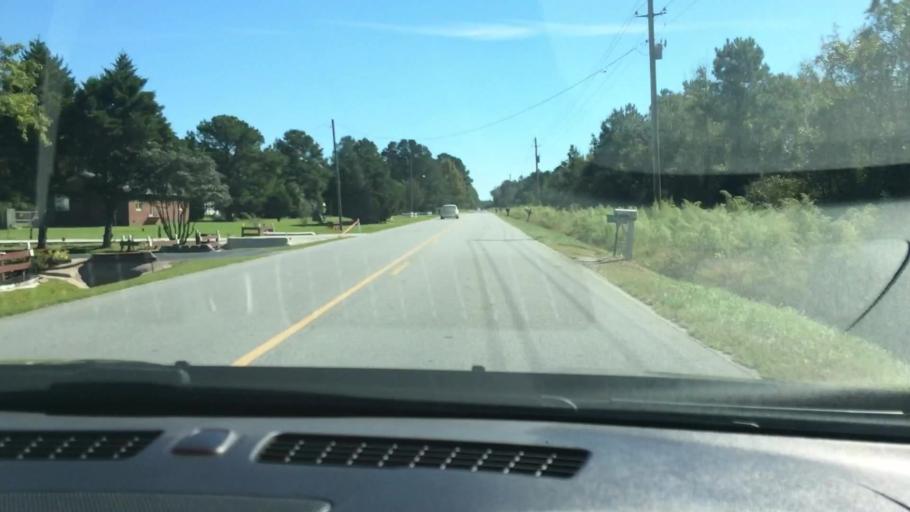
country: US
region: North Carolina
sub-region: Pitt County
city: Grifton
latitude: 35.4009
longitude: -77.4103
